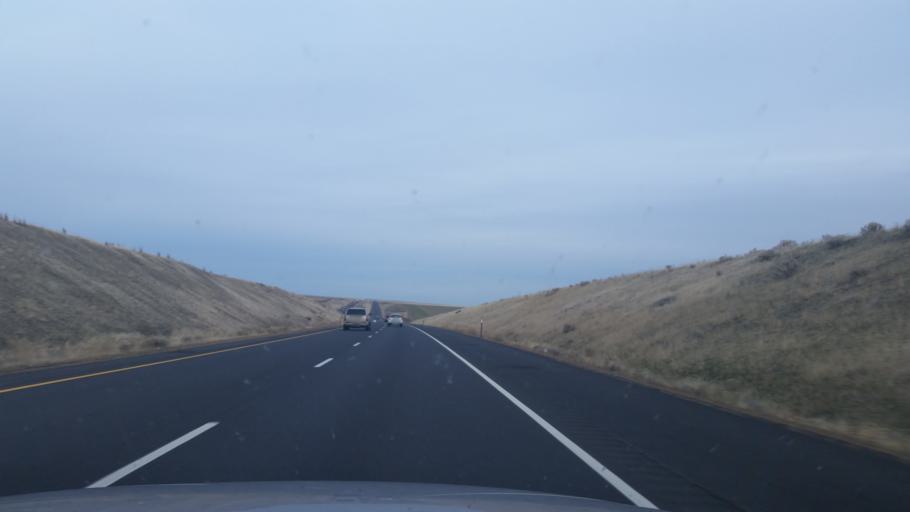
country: US
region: Washington
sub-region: Grant County
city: Warden
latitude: 47.0858
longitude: -118.8440
